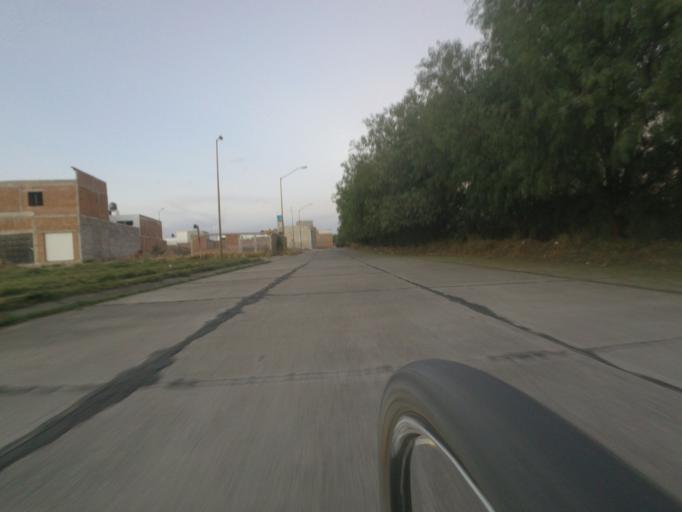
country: MX
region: Aguascalientes
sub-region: Aguascalientes
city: La Loma de los Negritos
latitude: 21.8484
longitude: -102.3310
